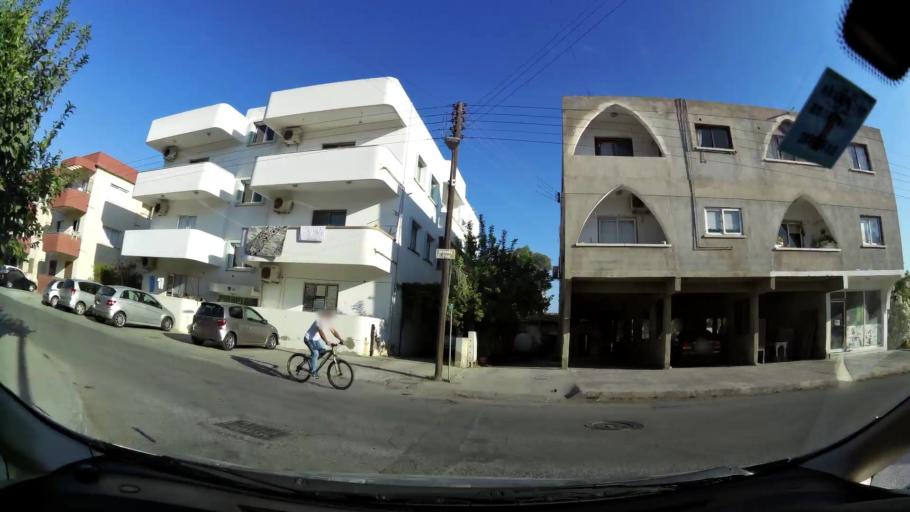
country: CY
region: Lefkosia
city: Nicosia
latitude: 35.2039
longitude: 33.3471
